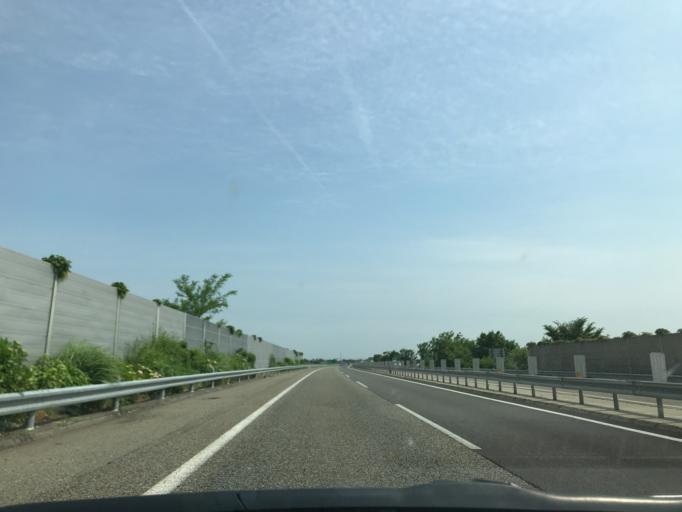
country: JP
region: Niigata
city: Mitsuke
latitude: 37.5786
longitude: 138.8890
